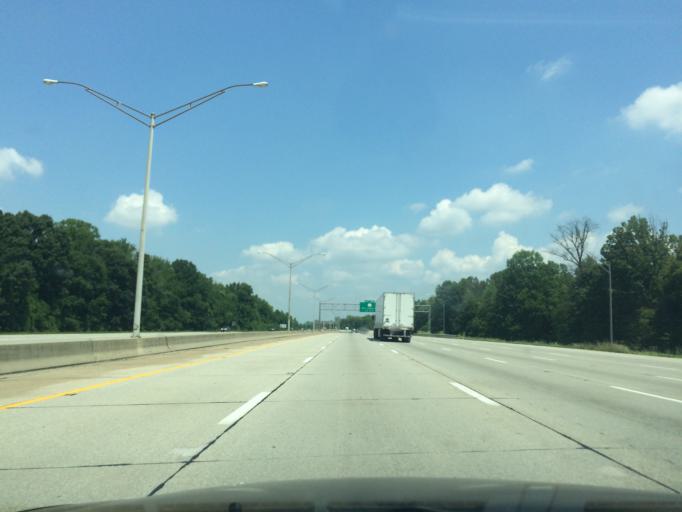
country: US
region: Kentucky
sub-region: Jefferson County
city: Heritage Creek
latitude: 38.1218
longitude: -85.7018
